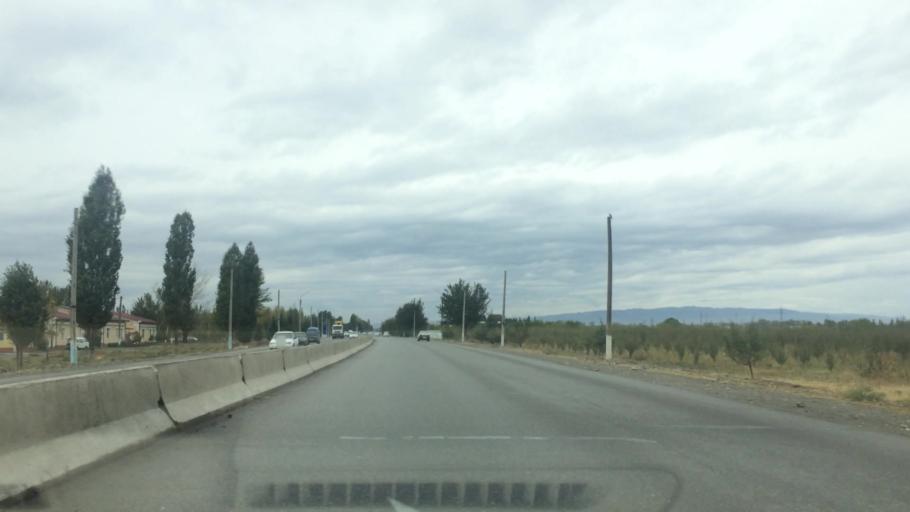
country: UZ
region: Jizzax
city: Jizzax
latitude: 40.0176
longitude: 67.6089
